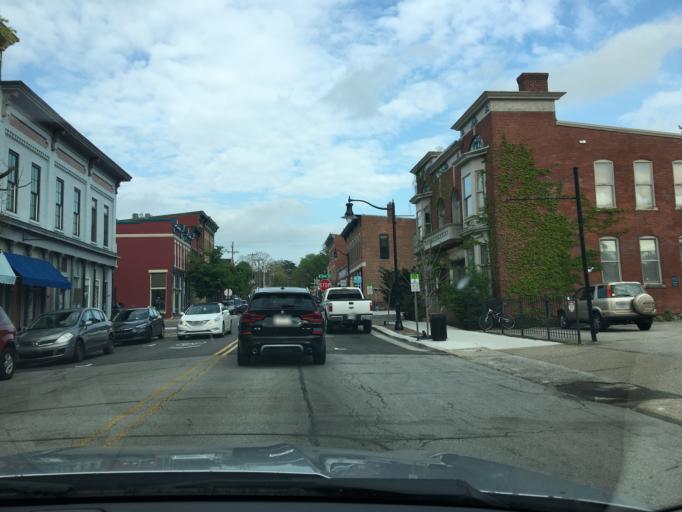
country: US
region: Indiana
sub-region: Tippecanoe County
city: Lafayette
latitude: 40.4191
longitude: -86.8864
